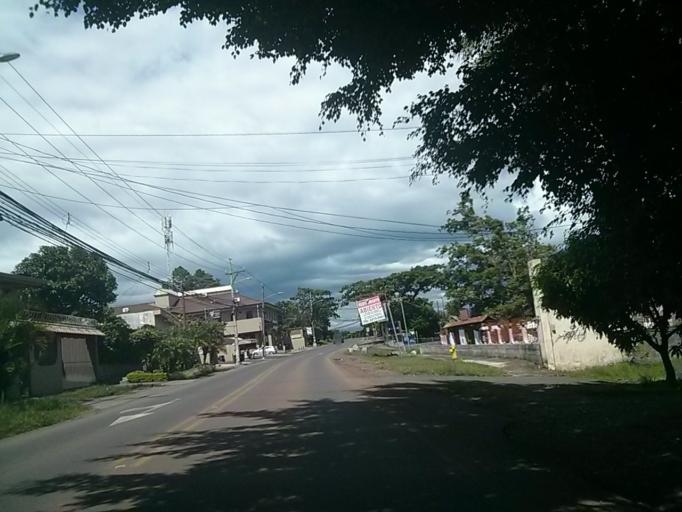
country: CR
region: San Jose
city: Santa Ana
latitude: 9.9535
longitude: -84.1663
